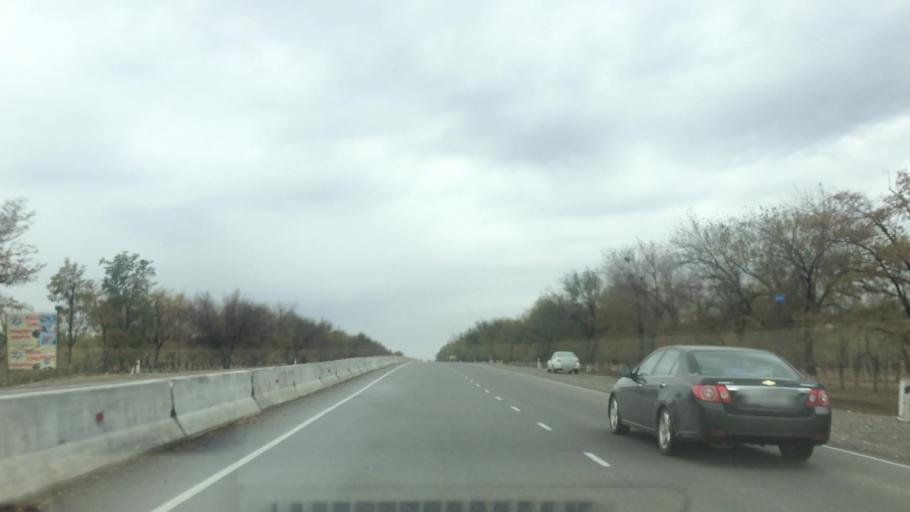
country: UZ
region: Samarqand
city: Bulung'ur
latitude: 39.9180
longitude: 67.5147
